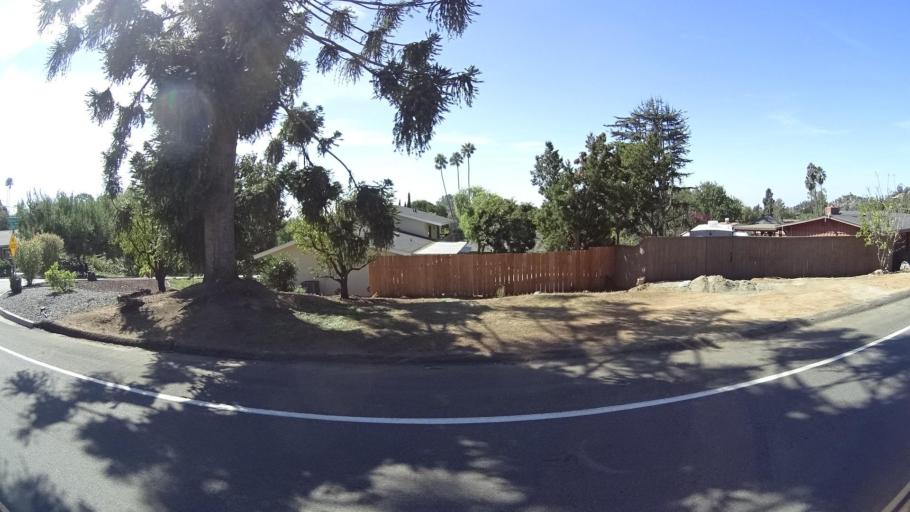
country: US
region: California
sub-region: San Diego County
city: Casa de Oro-Mount Helix
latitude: 32.7575
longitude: -116.9557
